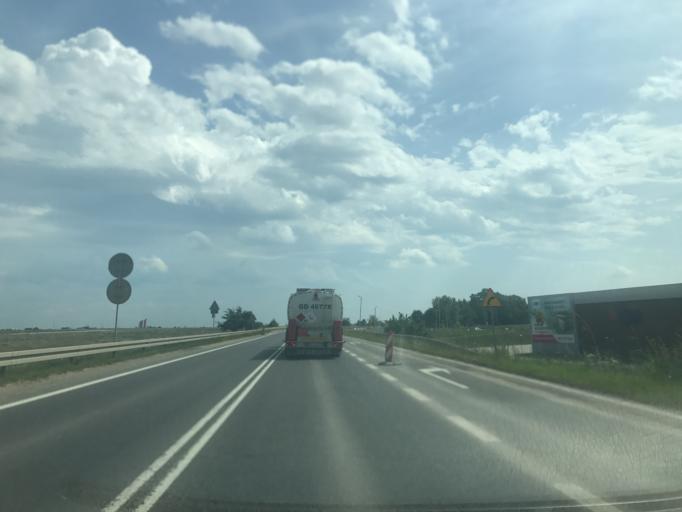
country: PL
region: Warmian-Masurian Voivodeship
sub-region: Powiat ostrodzki
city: Ostroda
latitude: 53.6868
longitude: 19.9960
